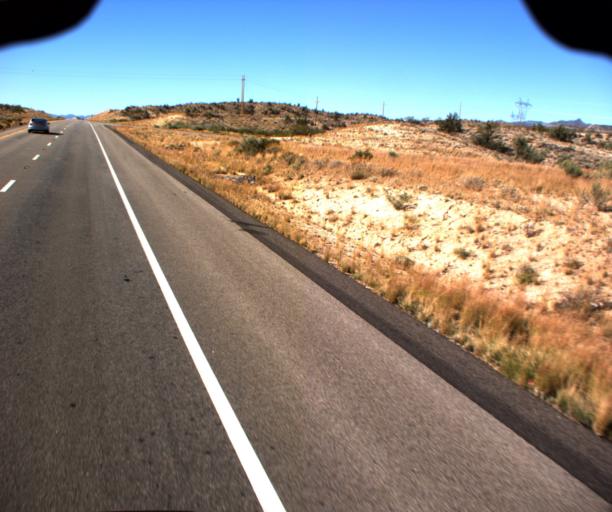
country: US
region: Arizona
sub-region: Mohave County
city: Kingman
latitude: 34.9100
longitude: -113.6569
